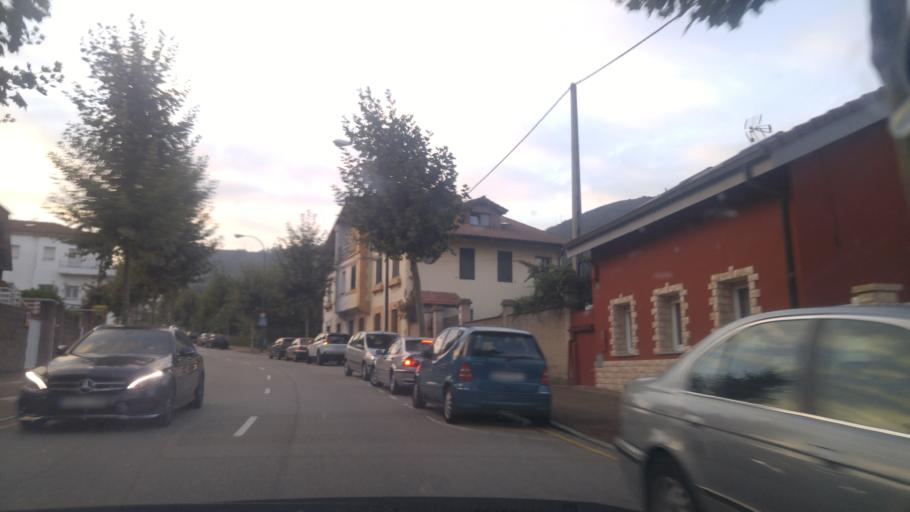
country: ES
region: Asturias
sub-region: Province of Asturias
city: Oviedo
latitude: 43.3721
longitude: -5.8604
